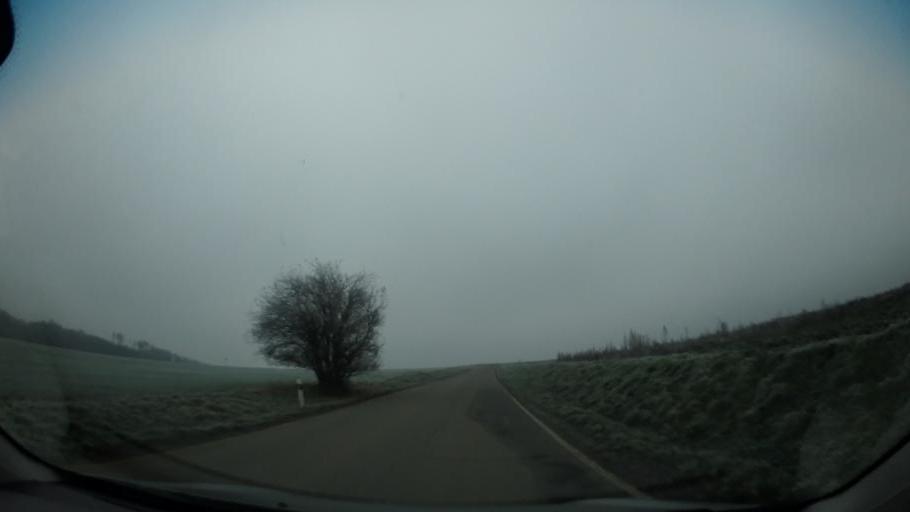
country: CZ
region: Vysocina
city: Mohelno
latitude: 49.1320
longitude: 16.2002
